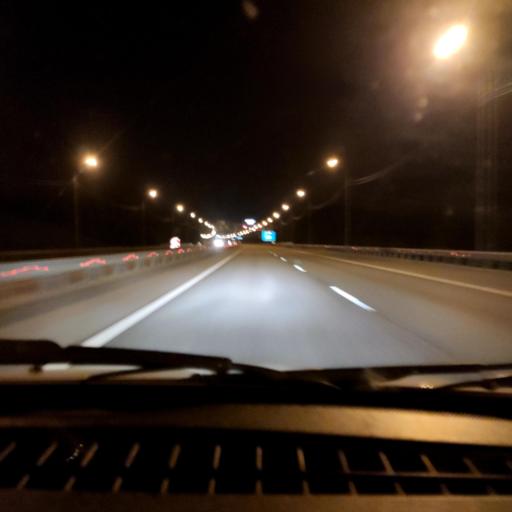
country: RU
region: Lipetsk
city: Zadonsk
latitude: 52.3638
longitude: 38.9313
